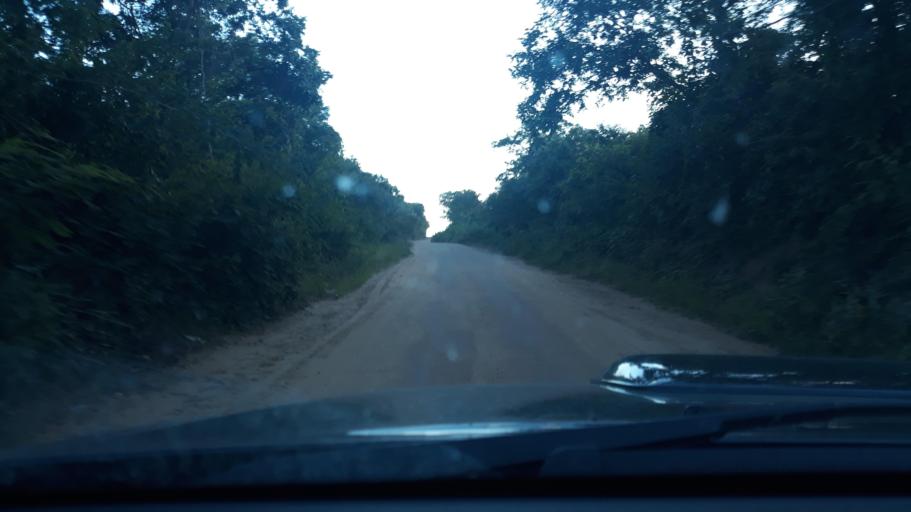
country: BR
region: Bahia
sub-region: Riacho De Santana
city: Riacho de Santana
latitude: -13.8157
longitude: -42.7230
